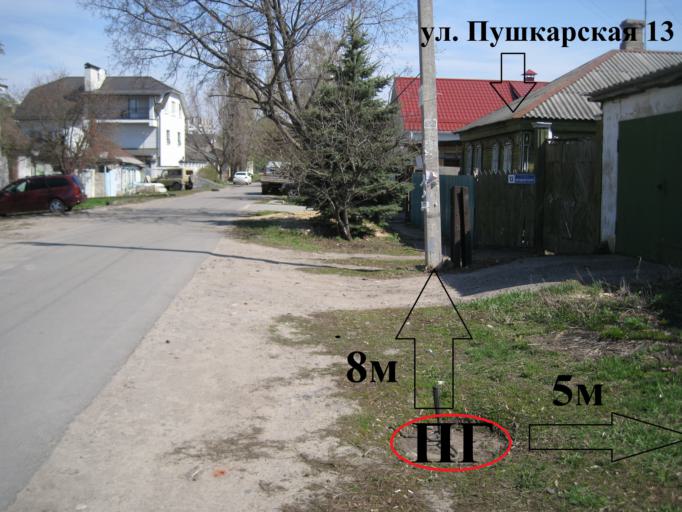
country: RU
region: Voronezj
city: Voronezh
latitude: 51.6453
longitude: 39.1776
